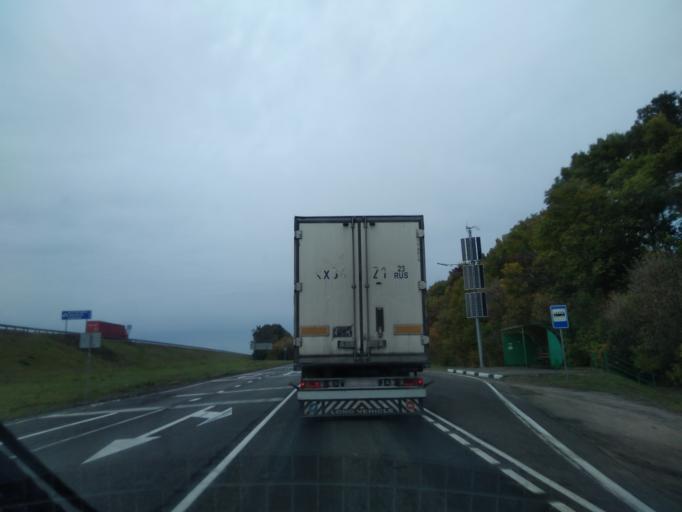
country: RU
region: Lipetsk
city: Zadonsk
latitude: 52.4607
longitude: 38.7752
